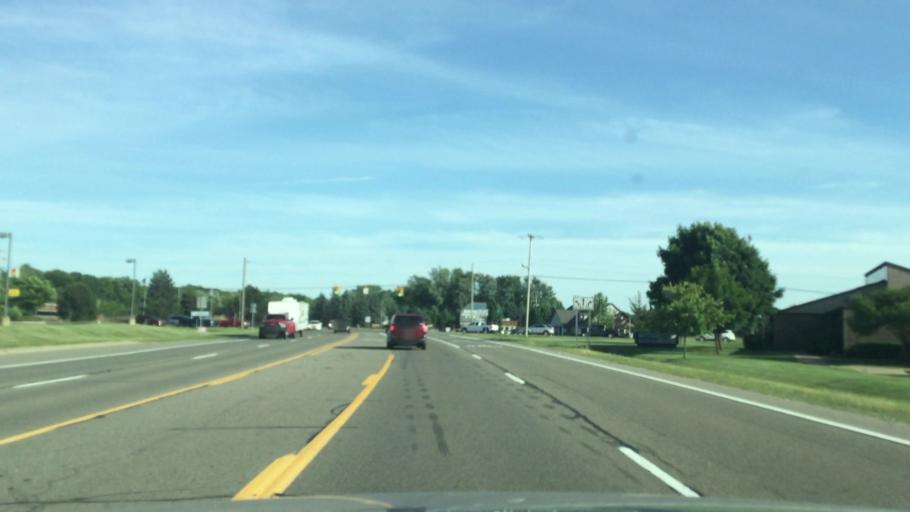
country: US
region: Michigan
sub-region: Genesee County
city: Davison
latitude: 43.0066
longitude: -83.5166
